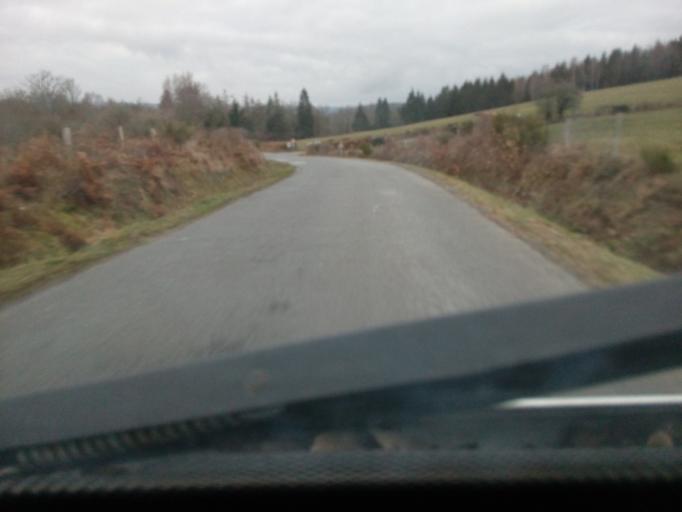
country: FR
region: Limousin
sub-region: Departement de la Creuse
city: Felletin
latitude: 45.8634
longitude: 2.2145
